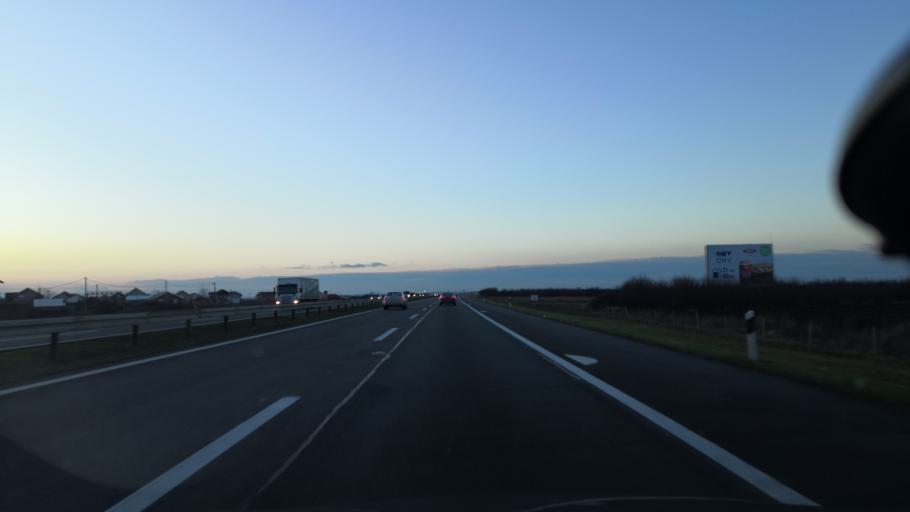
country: RS
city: Ugrinovci
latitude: 44.8589
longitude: 20.1633
